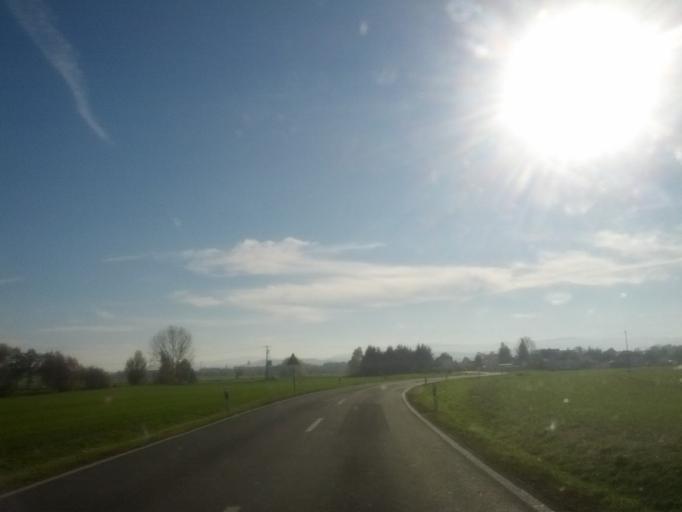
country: DE
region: Thuringia
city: Mechterstadt
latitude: 50.9336
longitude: 10.5480
